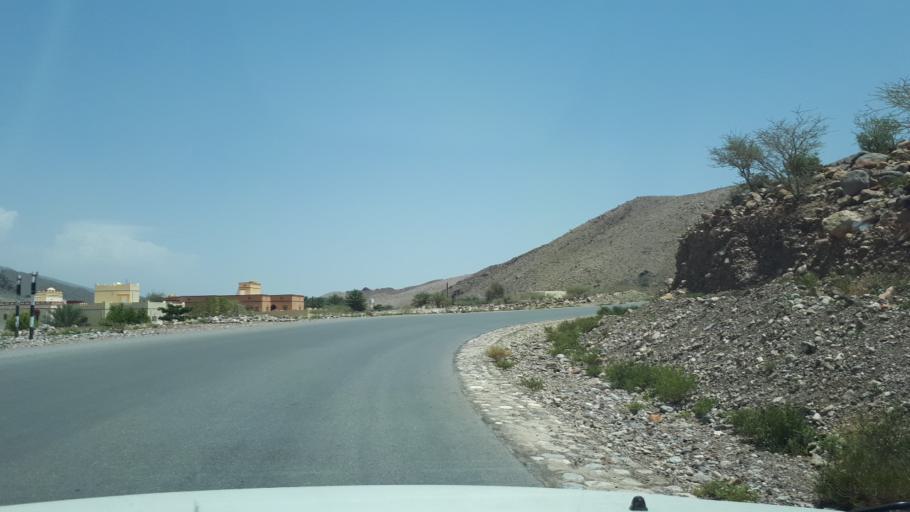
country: OM
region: Muhafazat ad Dakhiliyah
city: Bahla'
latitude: 23.1555
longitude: 57.1787
